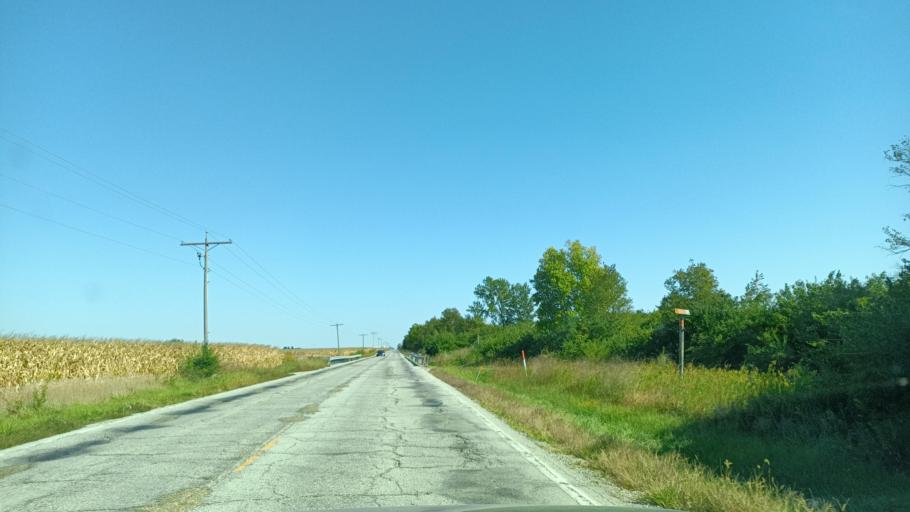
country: US
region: Illinois
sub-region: De Witt County
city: Farmer City
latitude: 40.2263
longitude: -88.5655
